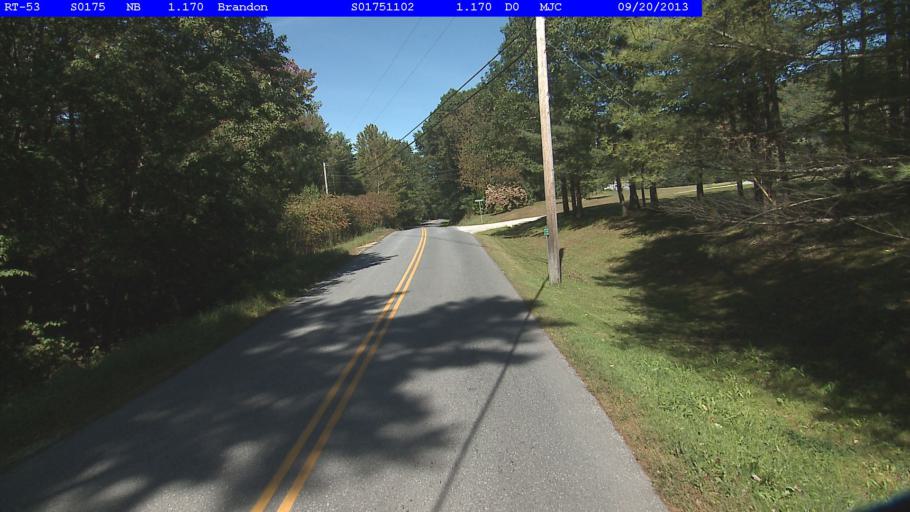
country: US
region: Vermont
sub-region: Rutland County
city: Brandon
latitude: 43.8436
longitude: -73.0568
